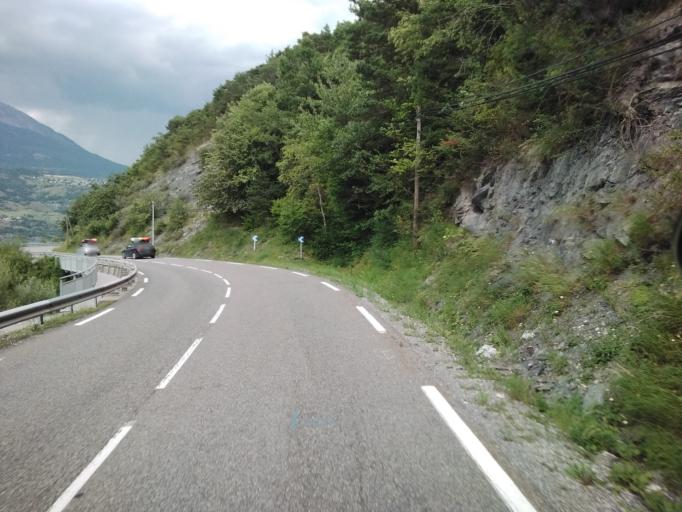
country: FR
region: Provence-Alpes-Cote d'Azur
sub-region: Departement des Hautes-Alpes
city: Embrun
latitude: 44.5215
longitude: 6.3936
